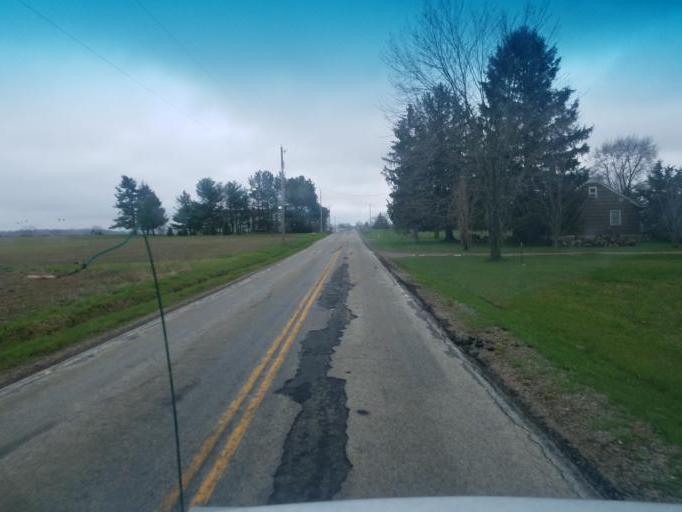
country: US
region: Ohio
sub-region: Richland County
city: Shelby
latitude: 40.9052
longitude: -82.6269
